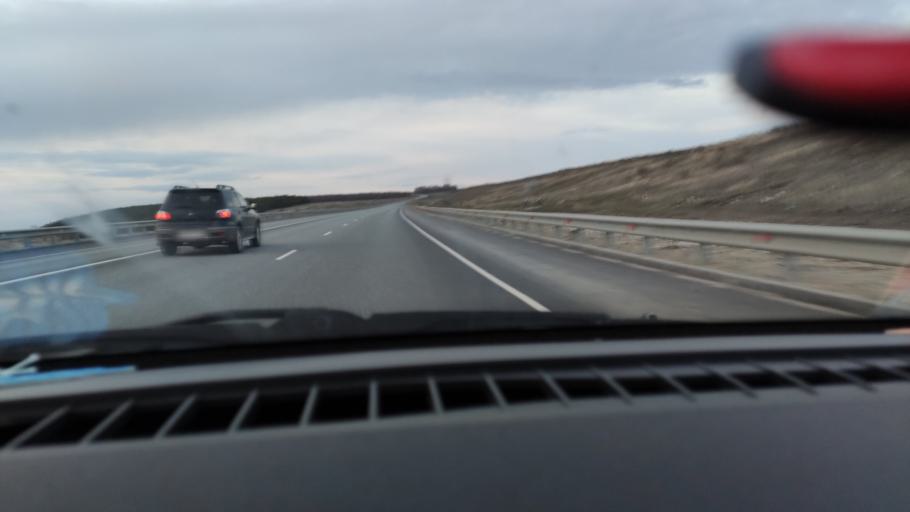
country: RU
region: Saratov
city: Yelshanka
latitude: 51.8785
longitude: 46.5077
